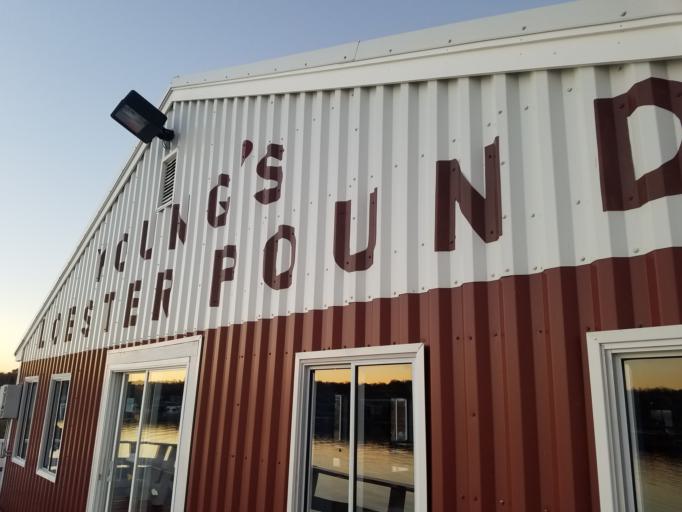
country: US
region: Maine
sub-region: Waldo County
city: Belfast
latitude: 44.4258
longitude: -69.0018
